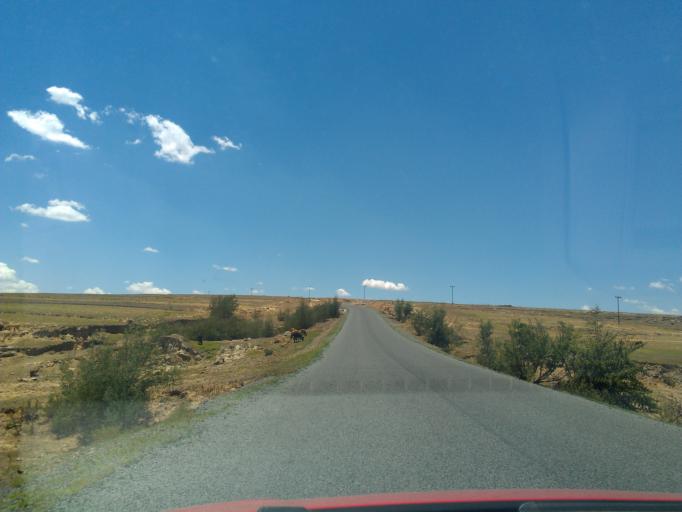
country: LS
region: Berea
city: Teyateyaneng
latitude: -29.1031
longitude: 27.8446
